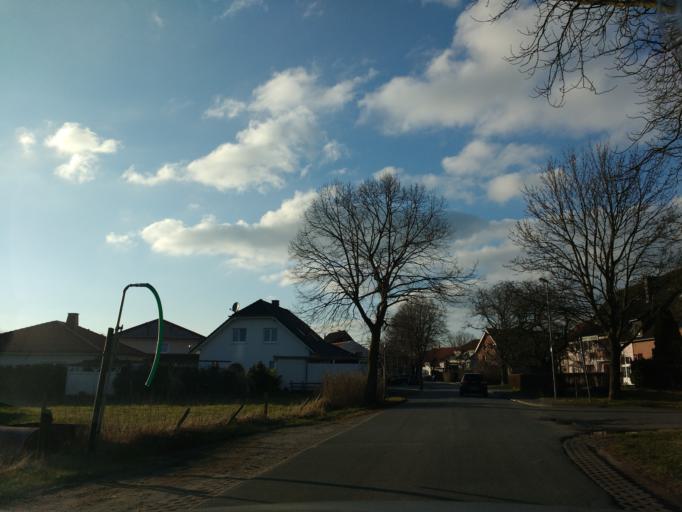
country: DE
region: North Rhine-Westphalia
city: Bad Lippspringe
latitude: 51.7770
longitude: 8.8279
